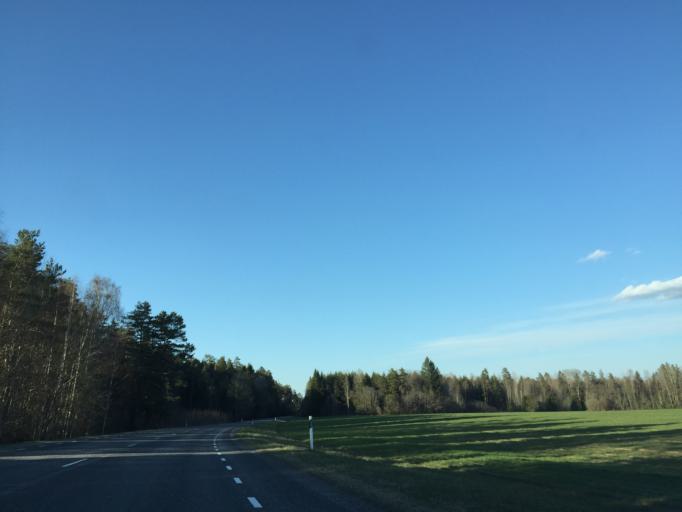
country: EE
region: Valgamaa
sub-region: Torva linn
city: Torva
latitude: 58.1183
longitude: 26.1318
